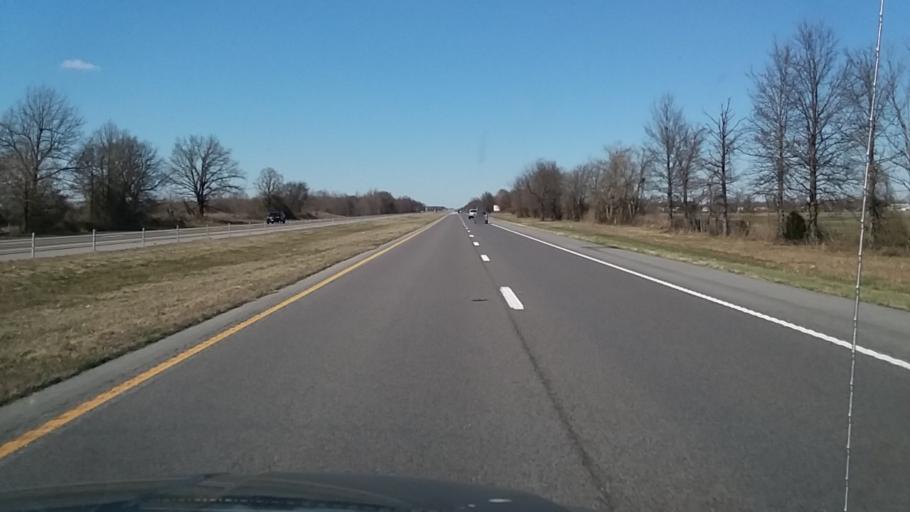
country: US
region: Missouri
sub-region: Scott County
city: Benton
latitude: 36.9877
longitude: -89.5346
